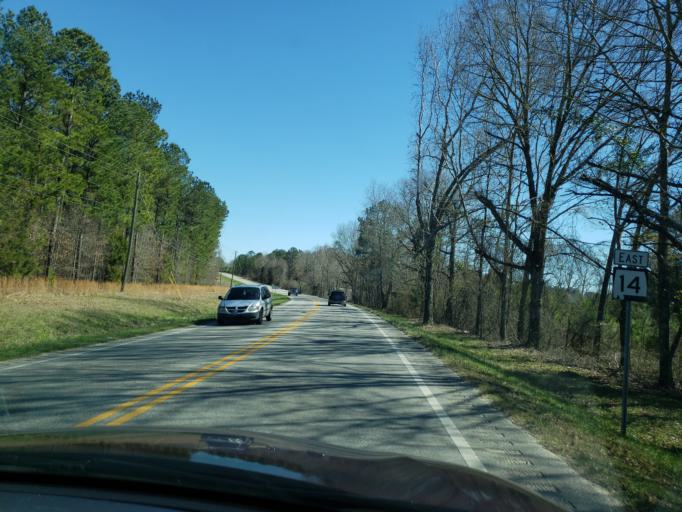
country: US
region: Alabama
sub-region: Lee County
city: Auburn
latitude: 32.5994
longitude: -85.5785
